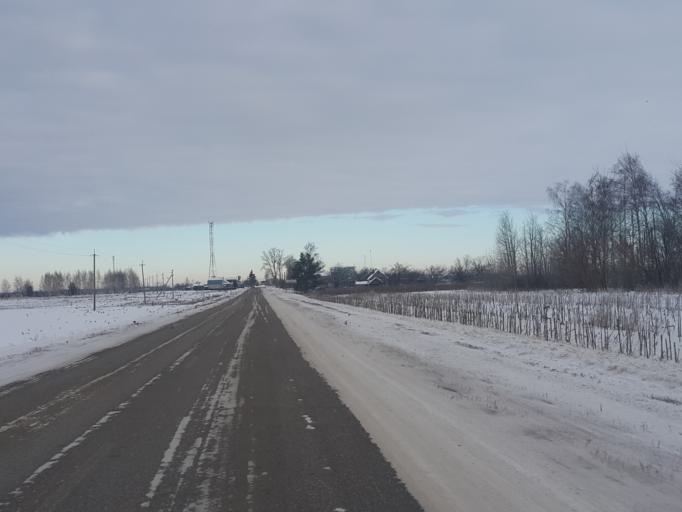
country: RU
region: Tambov
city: Rasskazovo
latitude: 52.8234
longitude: 41.8013
